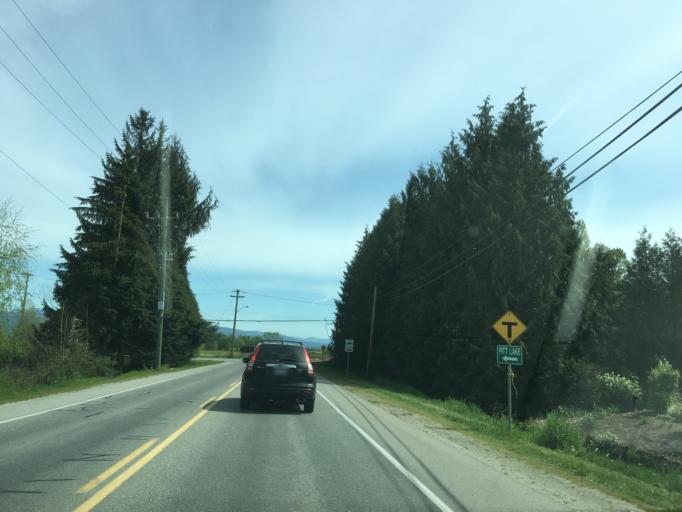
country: CA
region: British Columbia
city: Pitt Meadows
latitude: 49.2442
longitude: -122.6910
